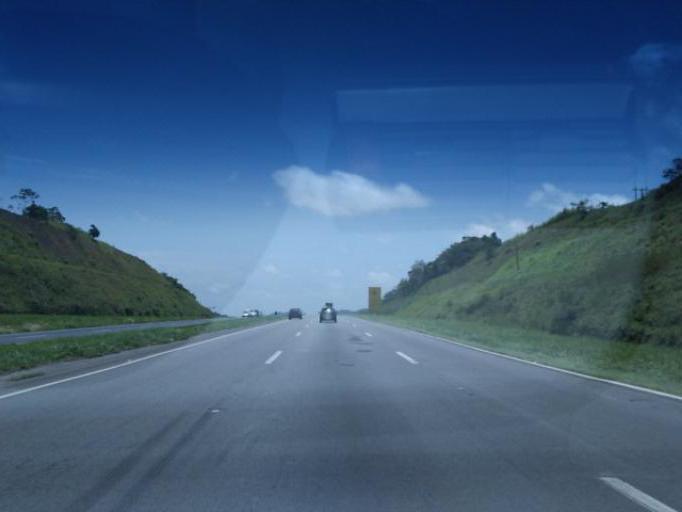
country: BR
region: Sao Paulo
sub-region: Juquia
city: Juquia
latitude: -24.3318
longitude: -47.6085
